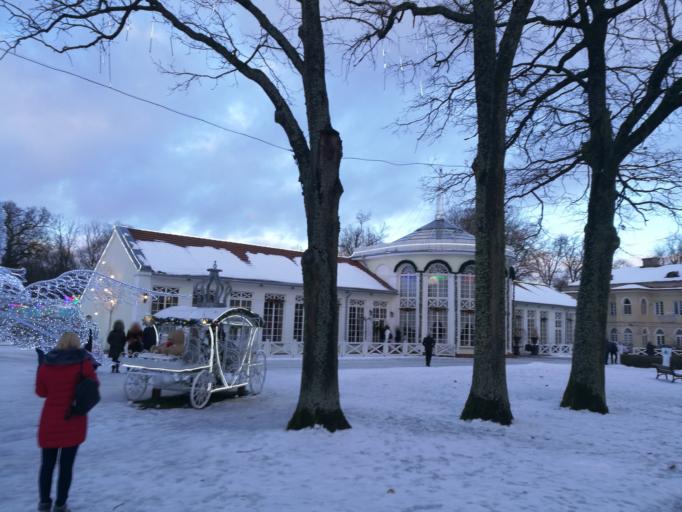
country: LT
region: Kauno apskritis
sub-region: Kauno rajonas
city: Akademija (Kaunas)
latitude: 54.9433
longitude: 23.7823
